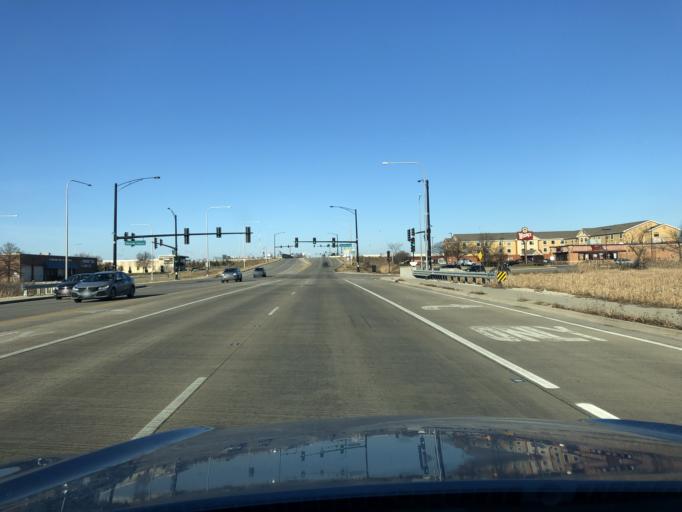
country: US
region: Illinois
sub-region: DuPage County
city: Itasca
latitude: 41.9840
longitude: -88.0314
